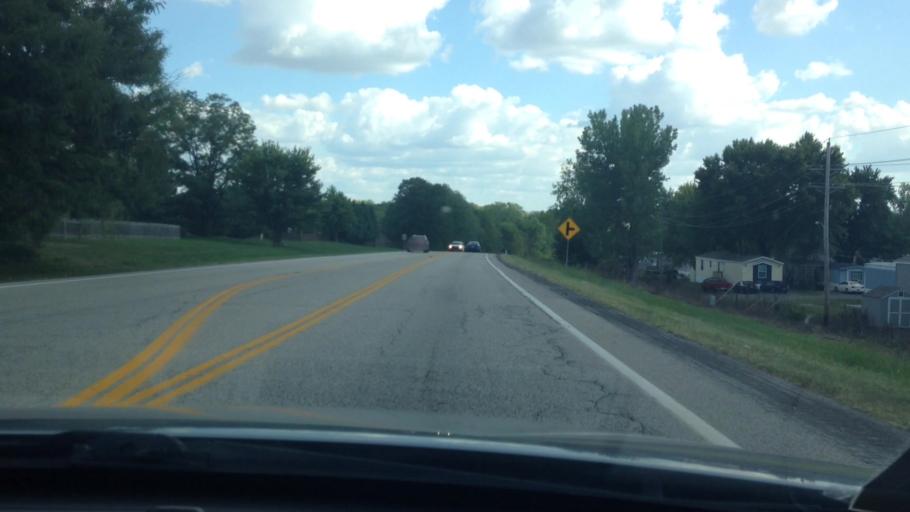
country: US
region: Missouri
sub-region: Clay County
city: Liberty
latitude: 39.2880
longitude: -94.4717
